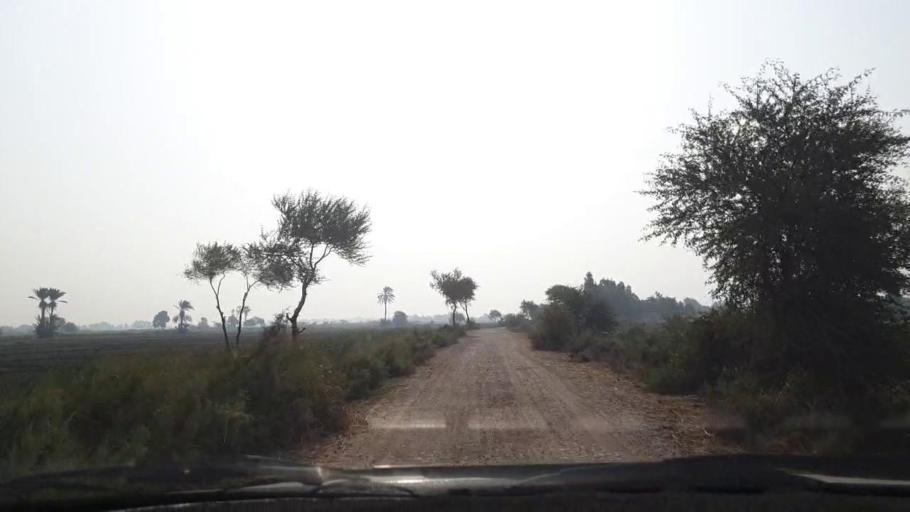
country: PK
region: Sindh
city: Tando Muhammad Khan
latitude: 25.0139
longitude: 68.4521
